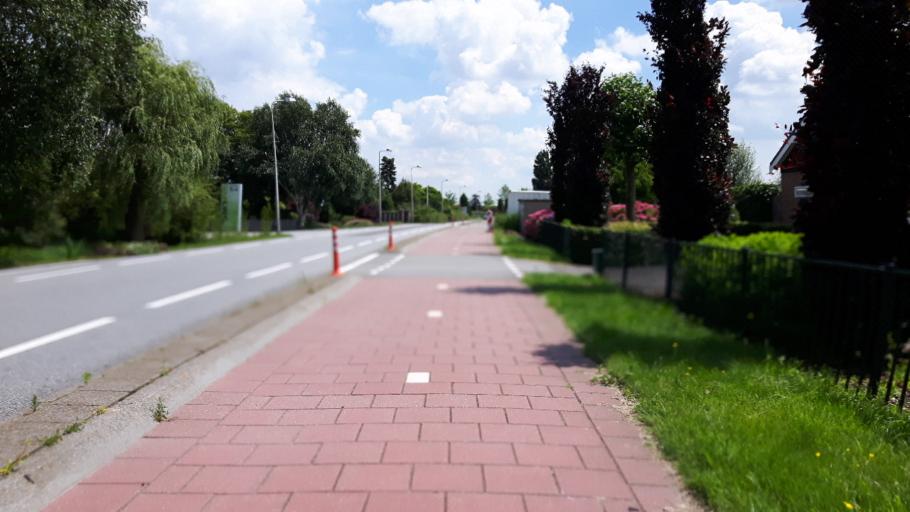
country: NL
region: South Holland
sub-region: Gemeente Boskoop
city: Boskoop
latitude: 52.0914
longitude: 4.6933
